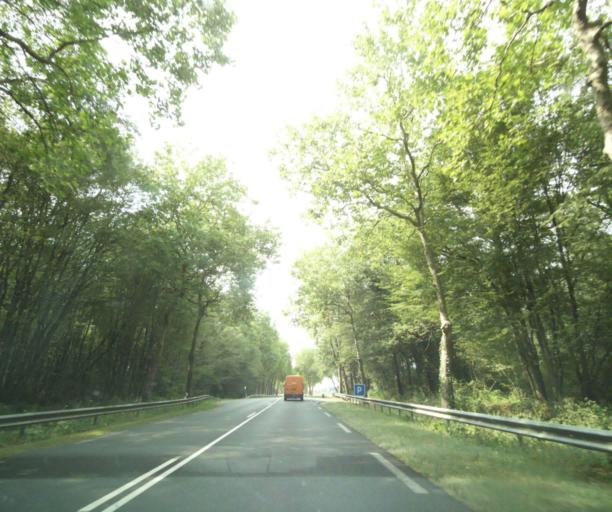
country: FR
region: Centre
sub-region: Departement d'Indre-et-Loire
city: Neuille-Pont-Pierre
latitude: 47.5317
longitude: 0.5652
